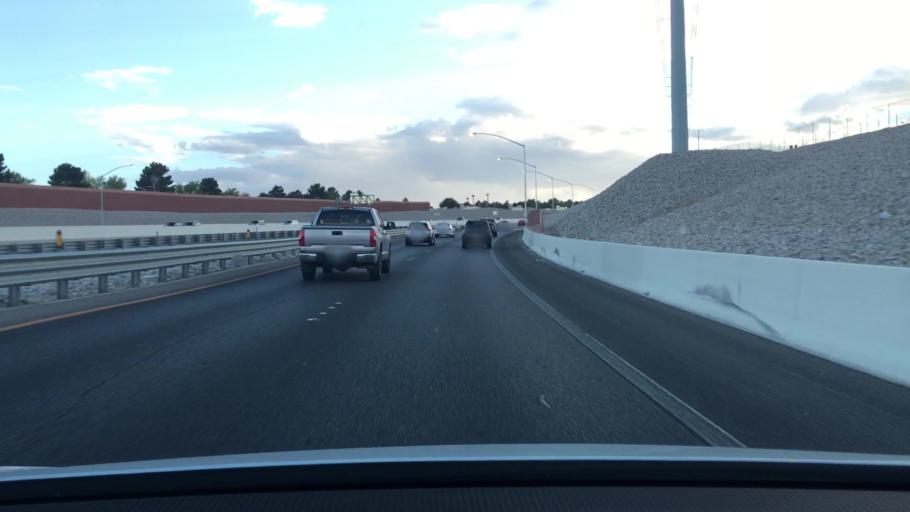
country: US
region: Nevada
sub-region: Clark County
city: Summerlin South
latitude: 36.2175
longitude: -115.3303
